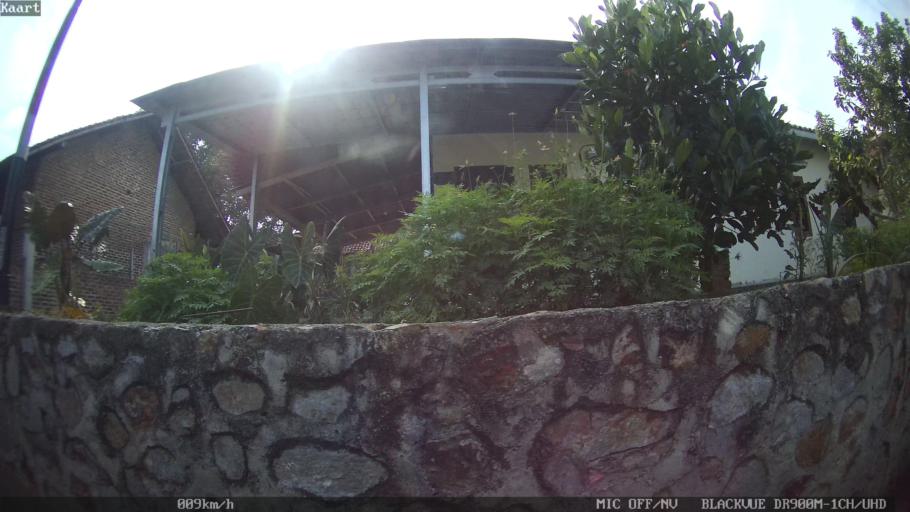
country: ID
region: Lampung
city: Kedaton
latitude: -5.3910
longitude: 105.2225
